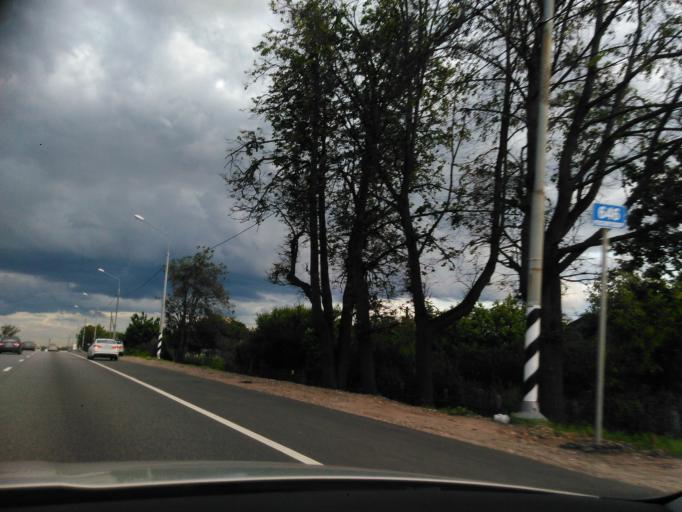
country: RU
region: Moskovskaya
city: Peshki
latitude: 56.1313
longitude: 37.0667
